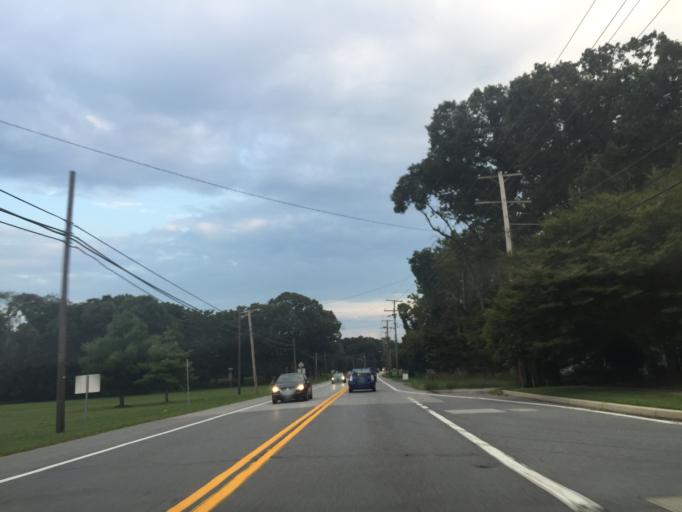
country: US
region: Maryland
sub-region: Anne Arundel County
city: Severn
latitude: 39.1275
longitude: -76.6892
